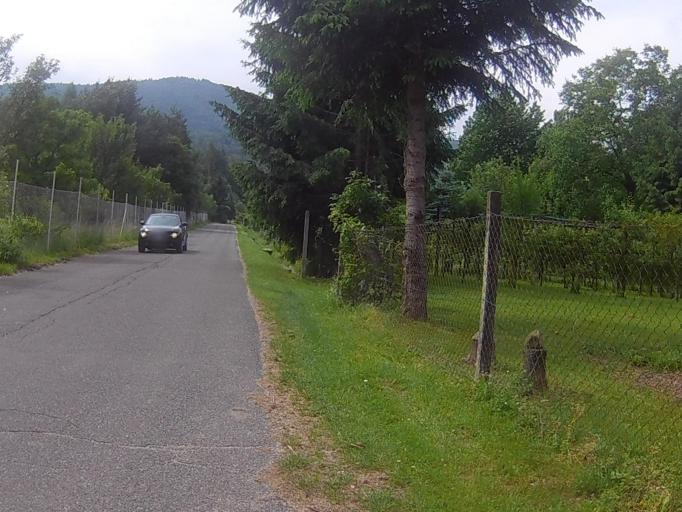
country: SI
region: Maribor
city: Pekre
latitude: 46.5348
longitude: 15.5832
